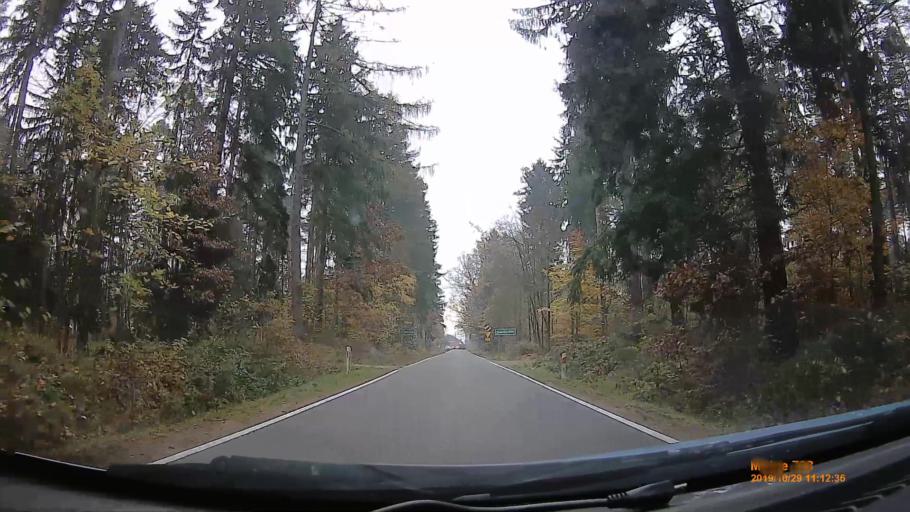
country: PL
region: Lower Silesian Voivodeship
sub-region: Powiat klodzki
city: Polanica-Zdroj
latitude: 50.4257
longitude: 16.5050
